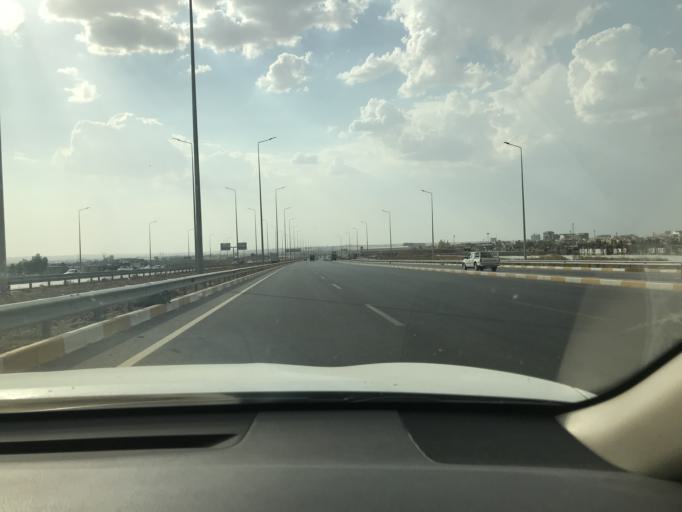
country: IQ
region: Arbil
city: Erbil
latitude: 36.1437
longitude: 43.9764
